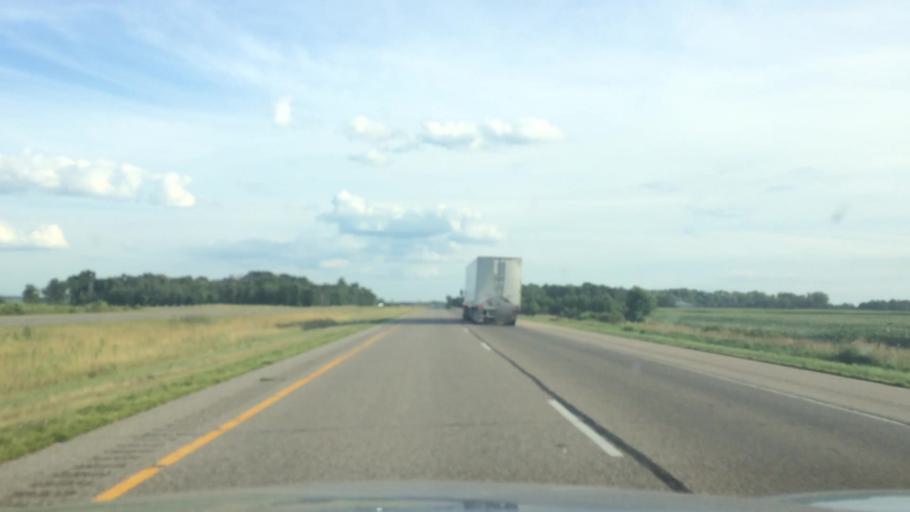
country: US
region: Wisconsin
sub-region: Portage County
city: Plover
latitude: 44.3817
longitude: -89.5200
